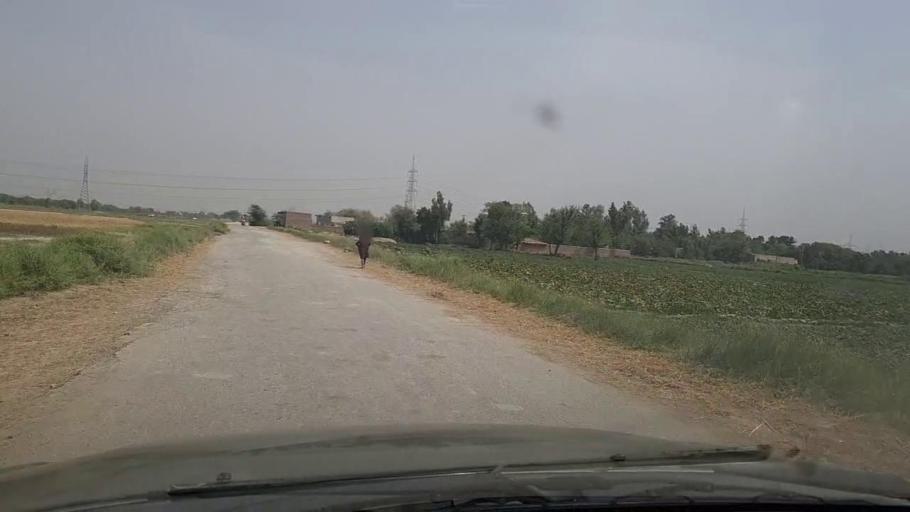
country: PK
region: Sindh
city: Shikarpur
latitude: 27.9247
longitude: 68.6688
